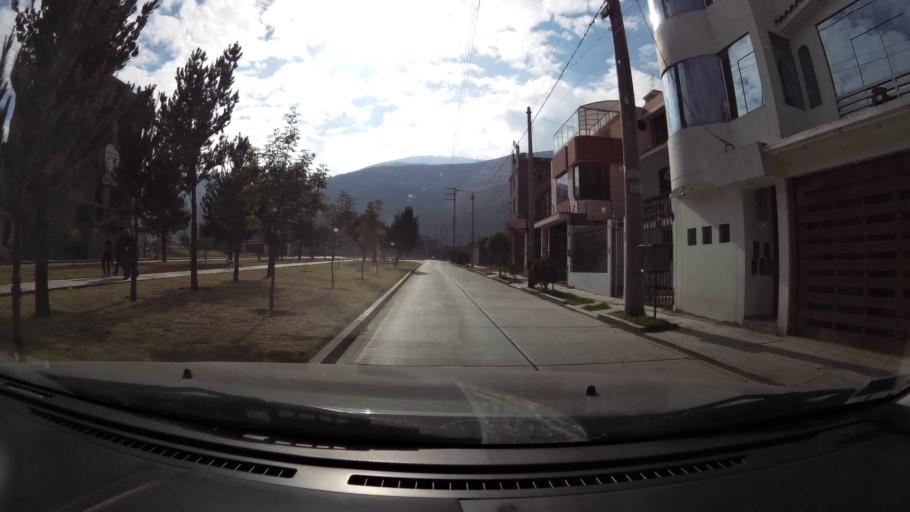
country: PE
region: Junin
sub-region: Provincia de Huancayo
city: Huancayo
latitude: -12.0492
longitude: -75.1915
